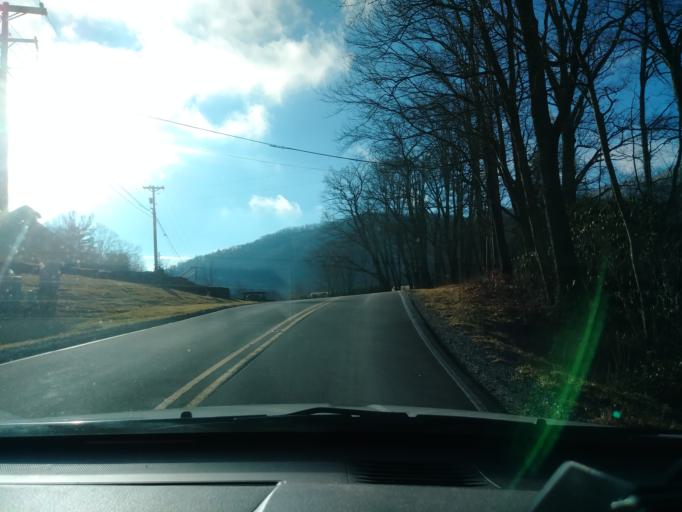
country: US
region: North Carolina
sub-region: Avery County
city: Banner Elk
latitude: 36.1754
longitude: -81.9191
